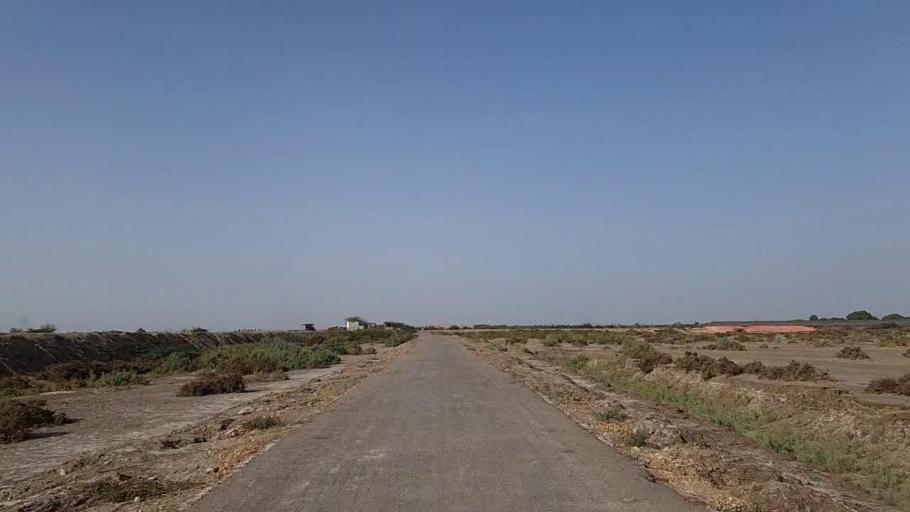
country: PK
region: Sindh
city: Jati
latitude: 24.3060
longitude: 68.1961
